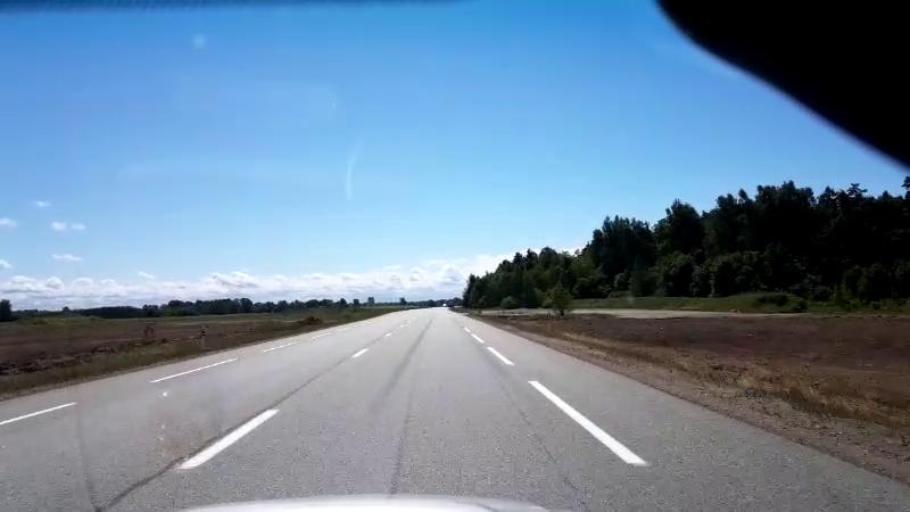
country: LV
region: Saulkrastu
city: Saulkrasti
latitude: 57.4119
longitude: 24.4314
